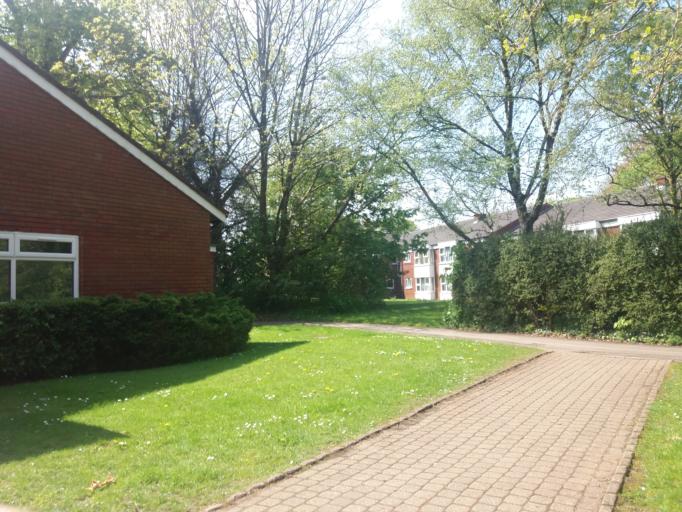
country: GB
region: England
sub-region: Lancashire
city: Euxton
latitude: 53.6609
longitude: -2.6462
